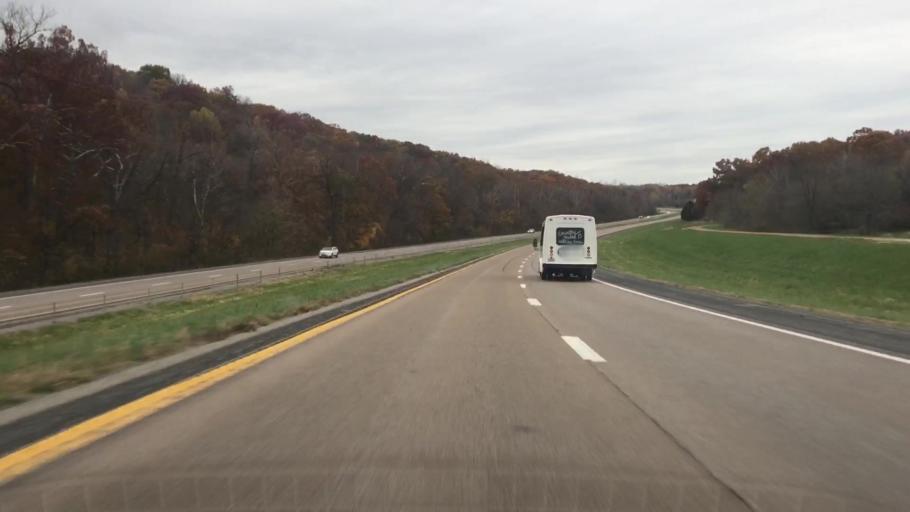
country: US
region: Missouri
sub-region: Cole County
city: Jefferson City
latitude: 38.6595
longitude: -92.2226
